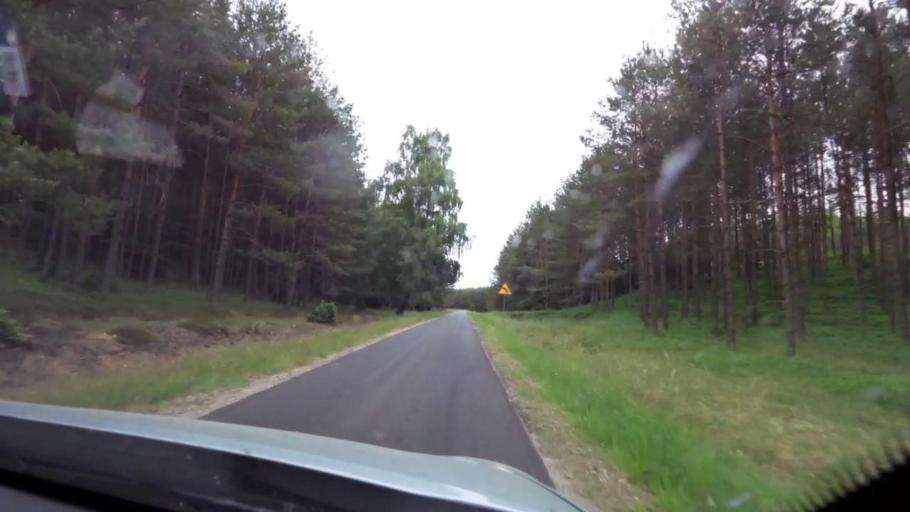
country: PL
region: Pomeranian Voivodeship
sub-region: Powiat bytowski
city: Trzebielino
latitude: 54.1962
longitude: 17.0326
